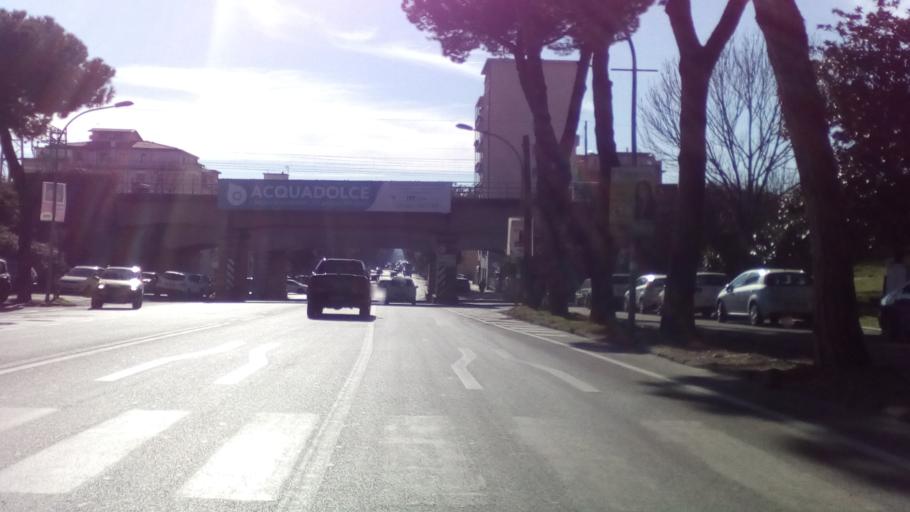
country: IT
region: Tuscany
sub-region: Provincia di Massa-Carrara
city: Carrara
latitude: 44.0532
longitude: 10.0608
